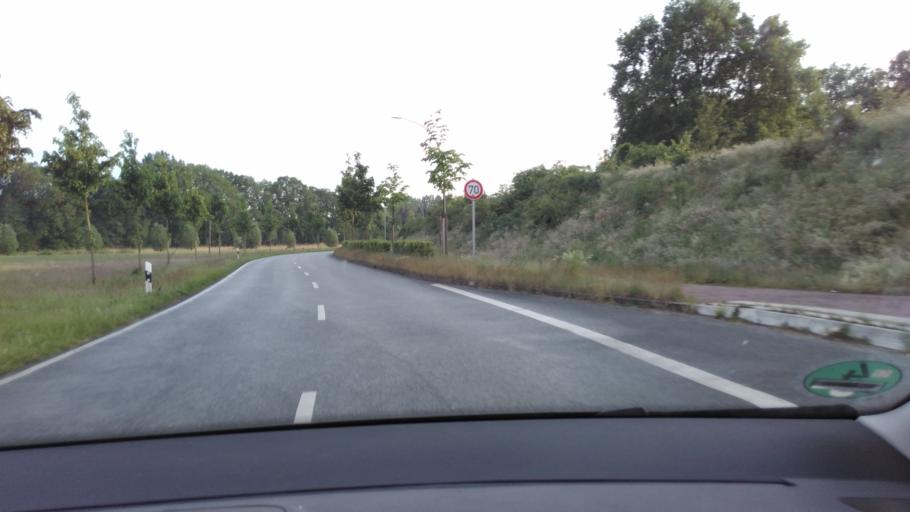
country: DE
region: North Rhine-Westphalia
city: Rietberg
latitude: 51.8255
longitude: 8.4473
